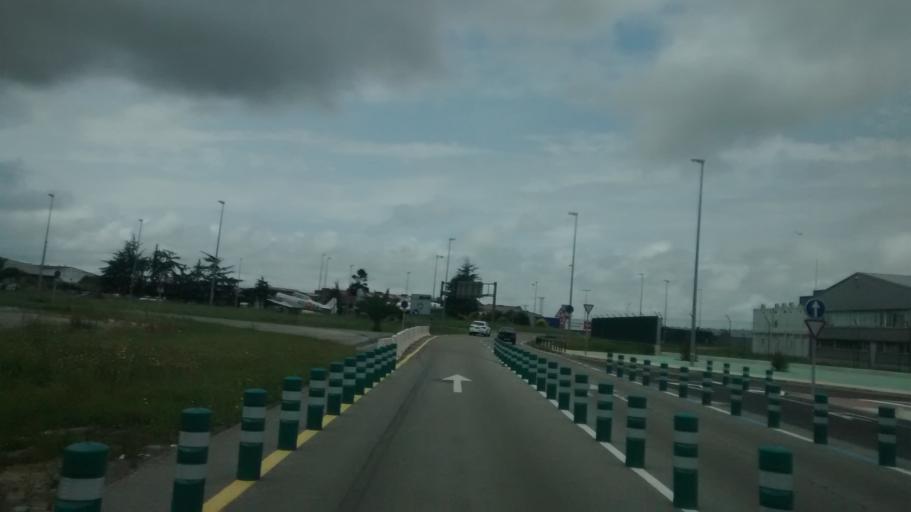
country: ES
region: Cantabria
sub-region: Provincia de Cantabria
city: El Astillero
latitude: 43.4235
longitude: -3.8260
